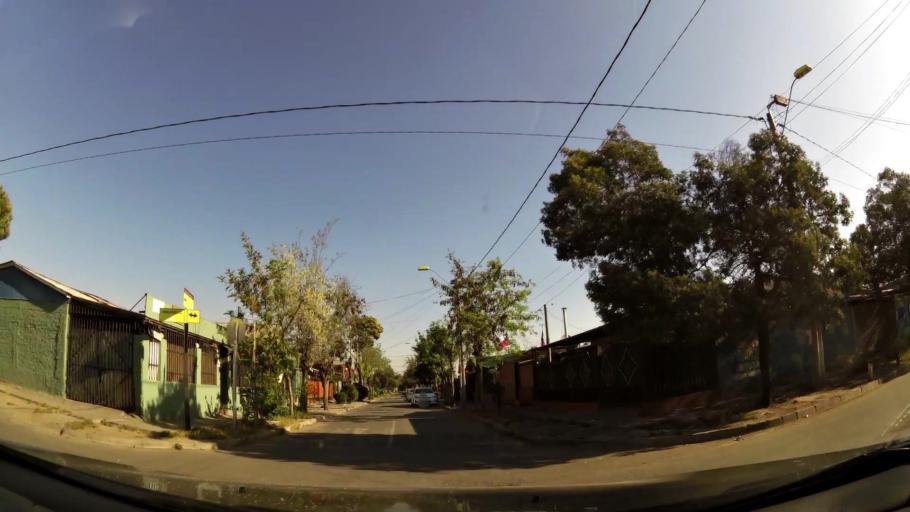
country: CL
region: Santiago Metropolitan
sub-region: Provincia de Santiago
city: La Pintana
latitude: -33.5809
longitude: -70.6561
